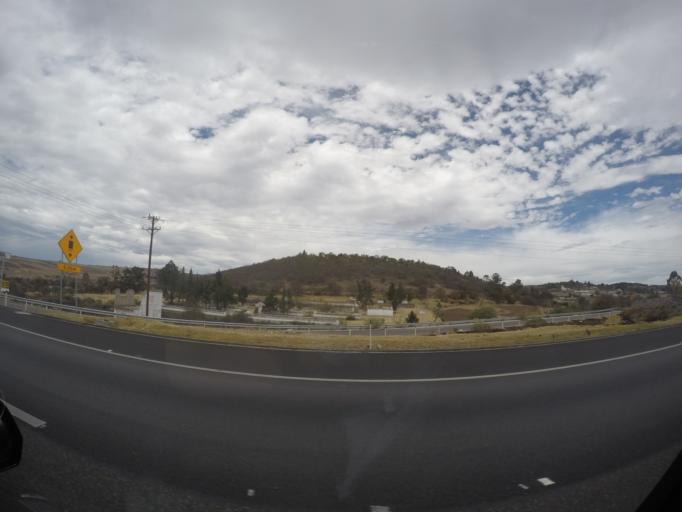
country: MX
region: Mexico
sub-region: Aculco
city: El Colorado
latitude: 20.0979
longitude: -99.6933
